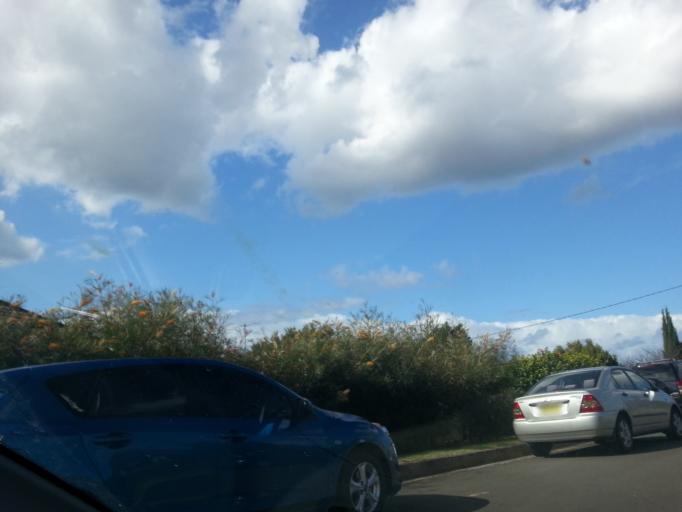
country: AU
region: New South Wales
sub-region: Wollongong
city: Keiraville
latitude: -34.4183
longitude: 150.8666
